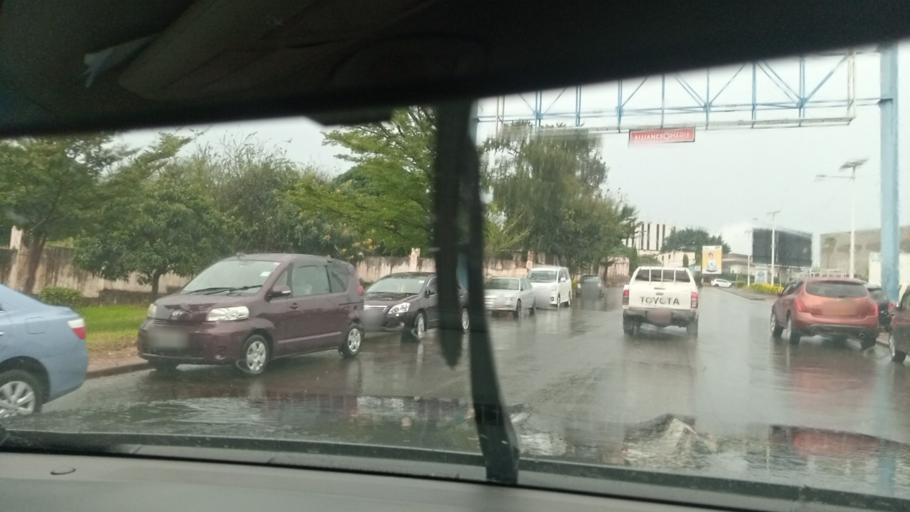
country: BI
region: Bujumbura Mairie
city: Bujumbura
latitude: -3.3810
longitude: 29.3585
